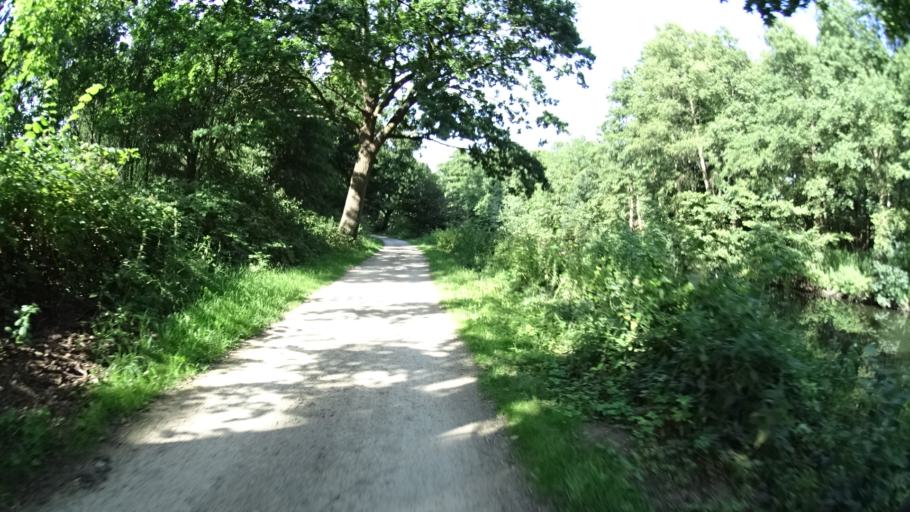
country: DE
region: Lower Saxony
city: Adendorf
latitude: 53.2691
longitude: 10.4229
